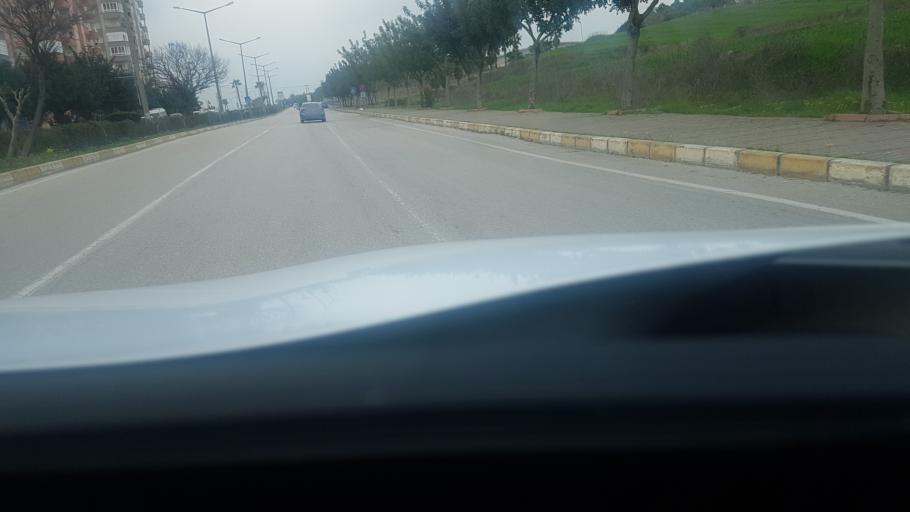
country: TR
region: Adana
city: Seyhan
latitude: 37.0541
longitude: 35.2503
